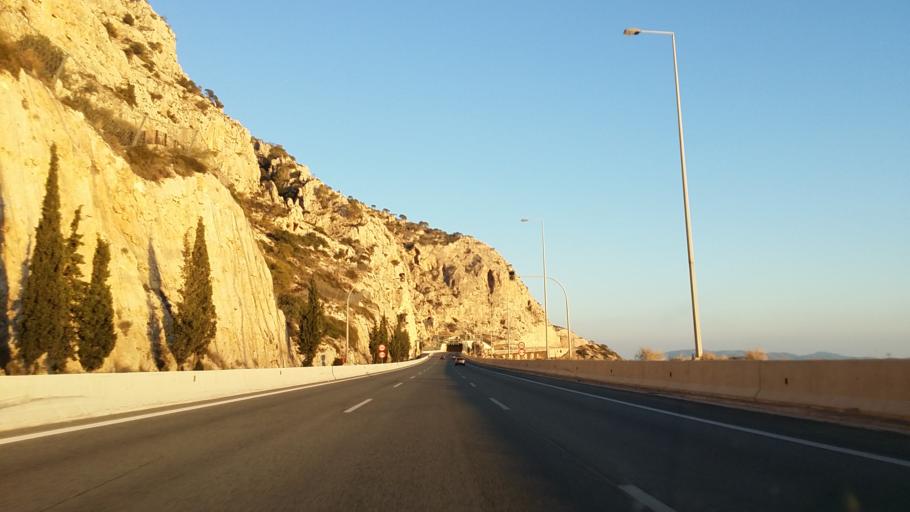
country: GR
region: Attica
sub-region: Nomarchia Dytikis Attikis
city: Kineta
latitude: 37.9792
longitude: 23.2738
